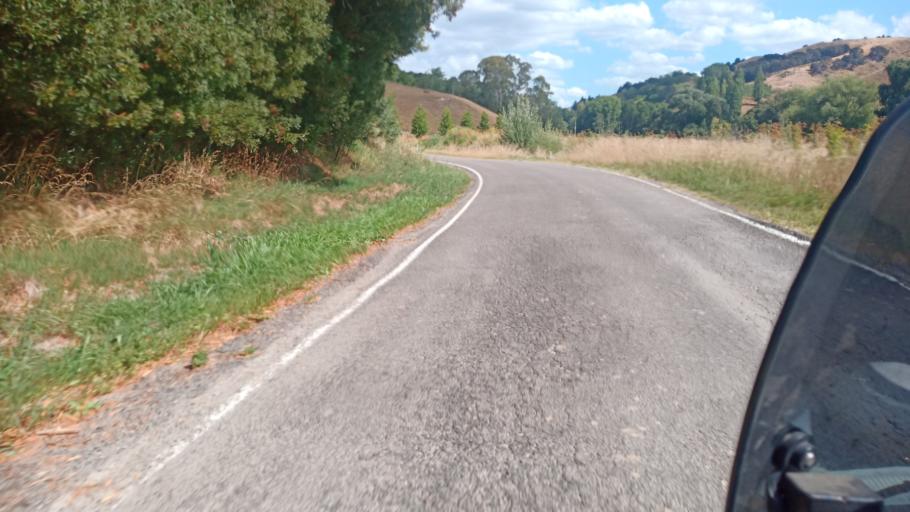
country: NZ
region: Gisborne
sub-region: Gisborne District
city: Gisborne
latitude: -38.5962
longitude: 177.7769
